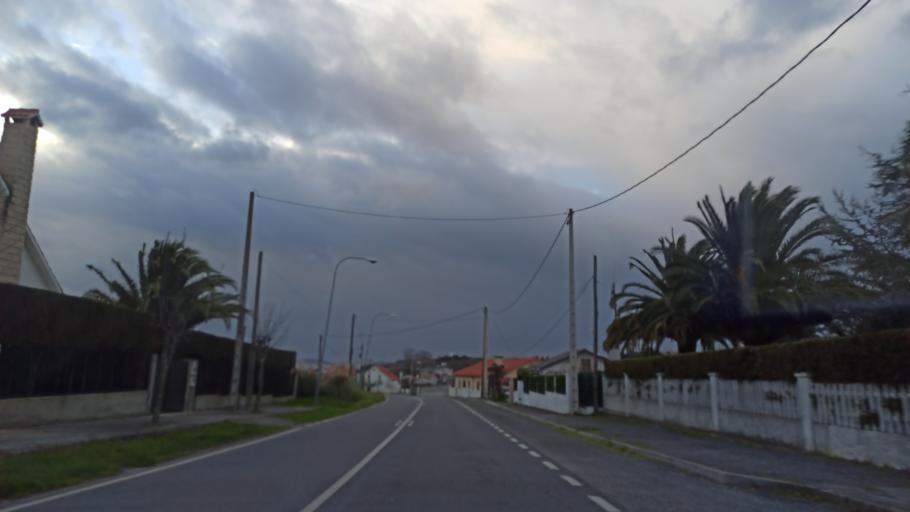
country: ES
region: Galicia
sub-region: Provincia da Coruna
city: Oleiros
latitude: 43.3821
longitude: -8.3290
